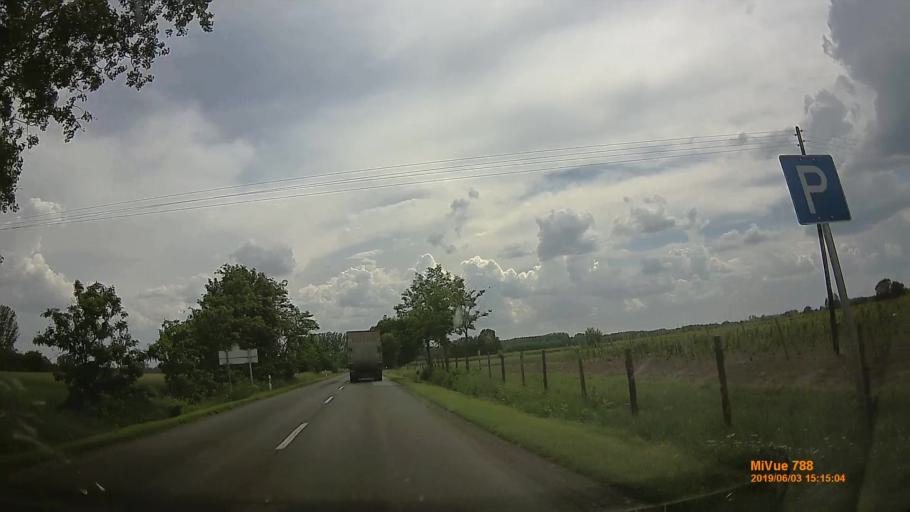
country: HU
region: Bacs-Kiskun
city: Orgovany
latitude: 46.7255
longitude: 19.5559
